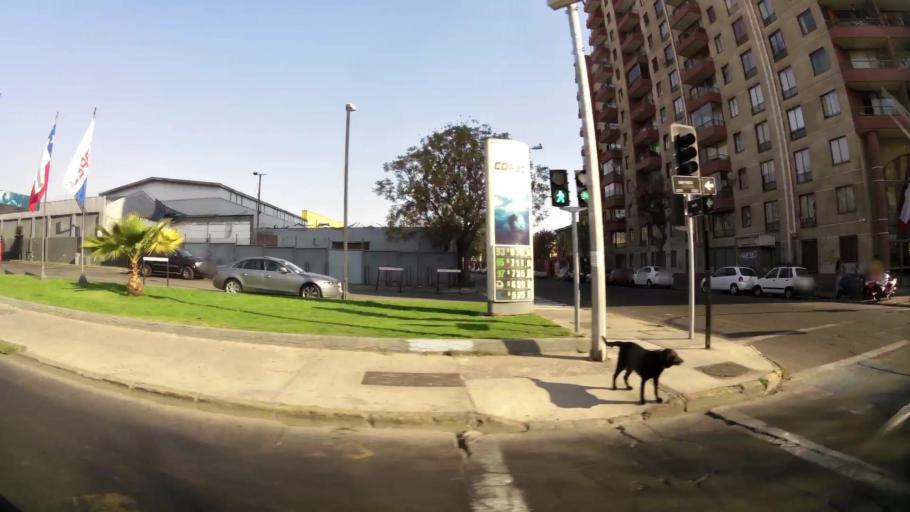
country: CL
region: Santiago Metropolitan
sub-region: Provincia de Santiago
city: Santiago
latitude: -33.4349
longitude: -70.6648
